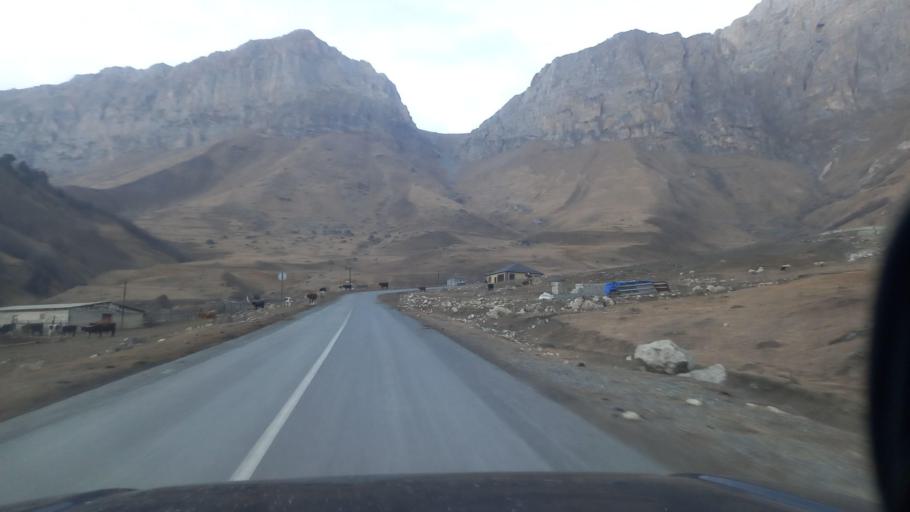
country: RU
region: Ingushetiya
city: Dzhayrakh
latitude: 42.8195
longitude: 44.8160
